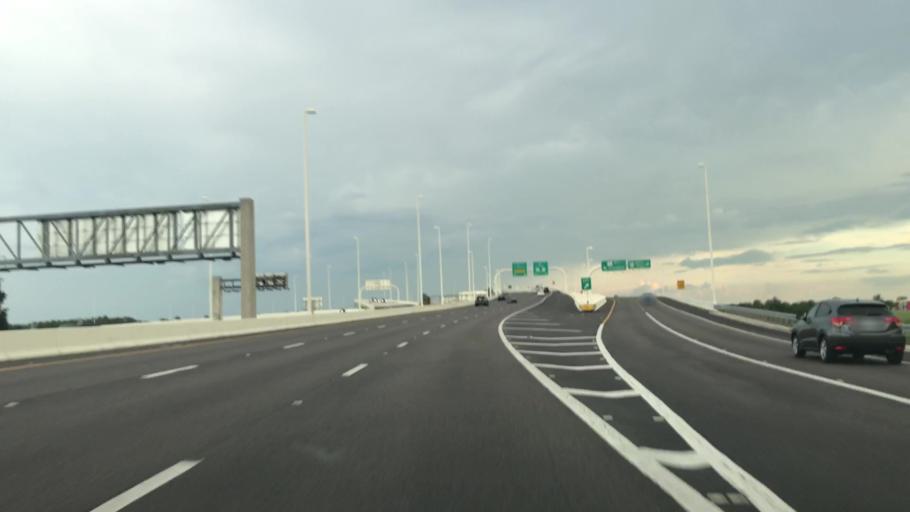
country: US
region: Florida
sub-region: Hillsborough County
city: Town 'n' Country
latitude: 27.9639
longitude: -82.5394
